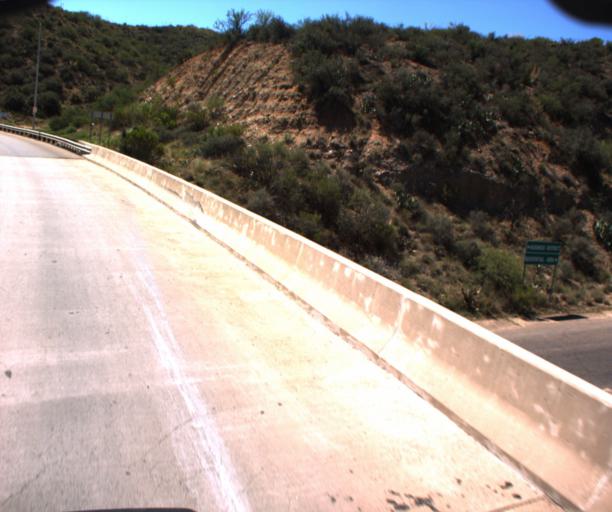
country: US
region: Arizona
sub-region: Gila County
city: Globe
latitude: 33.3923
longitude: -110.7876
